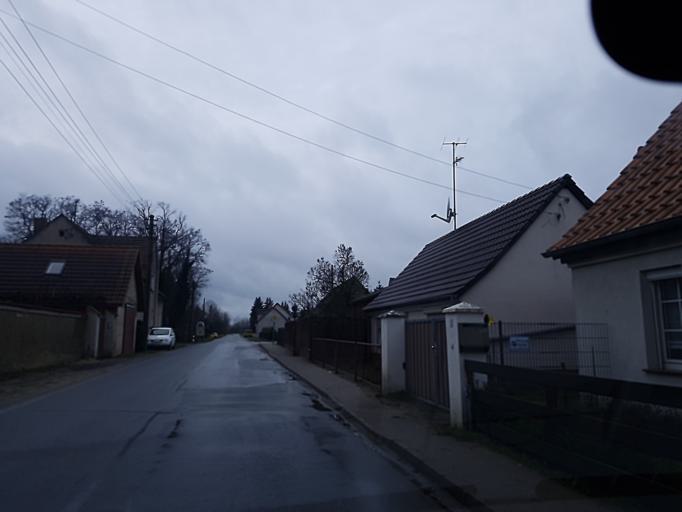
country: DE
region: Brandenburg
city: Finsterwalde
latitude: 51.6124
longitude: 13.7136
